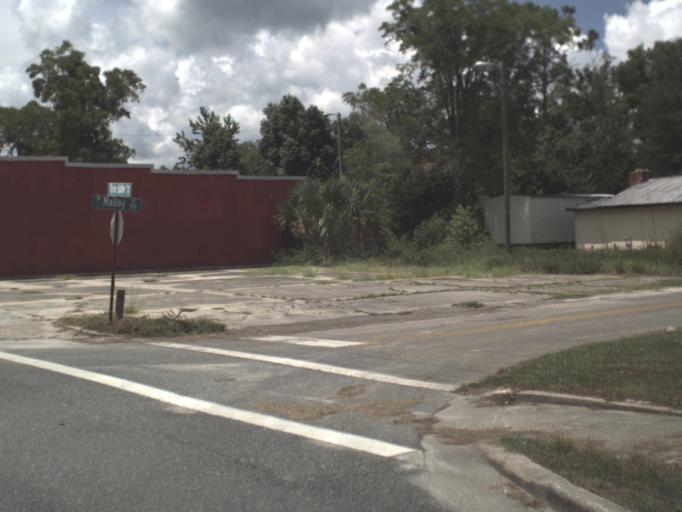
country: US
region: Florida
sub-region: Taylor County
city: Perry
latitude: 30.1133
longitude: -83.5893
